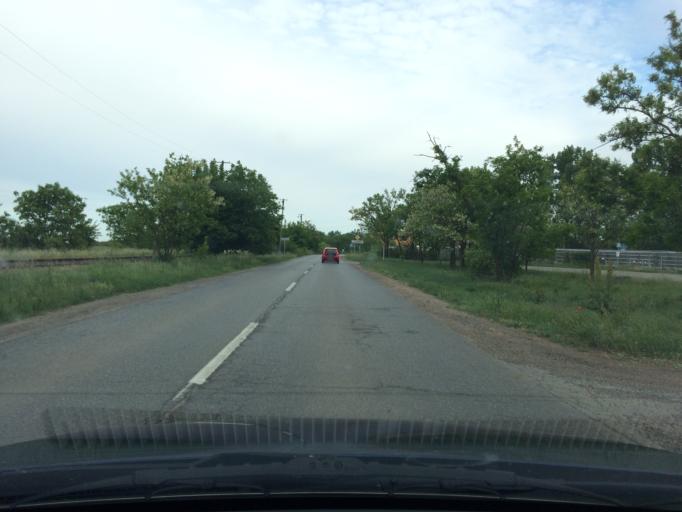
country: HU
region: Szabolcs-Szatmar-Bereg
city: Tiszavasvari
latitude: 47.9407
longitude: 21.3788
